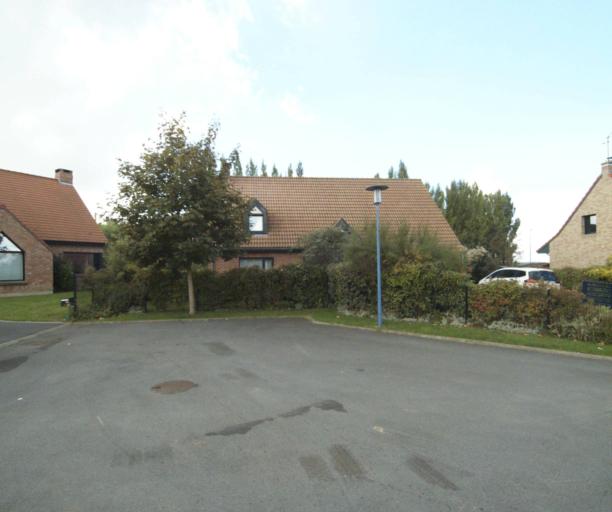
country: FR
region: Nord-Pas-de-Calais
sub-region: Departement du Nord
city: Herlies
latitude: 50.5799
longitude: 2.8498
